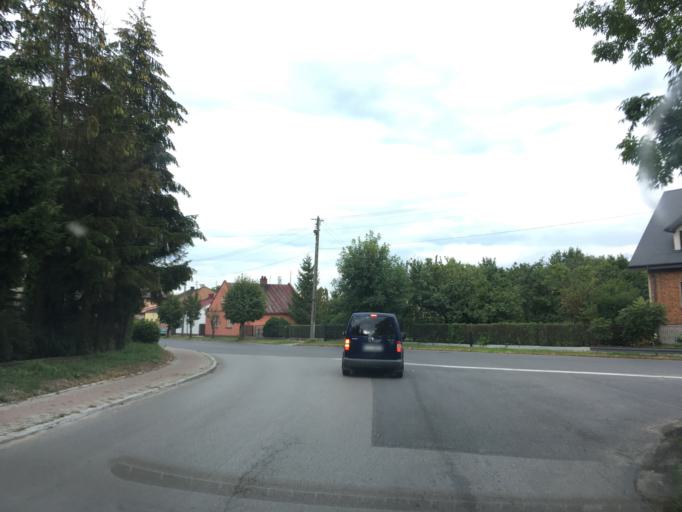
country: PL
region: Silesian Voivodeship
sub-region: Powiat zawiercianski
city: Szczekociny
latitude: 50.6219
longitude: 19.8160
